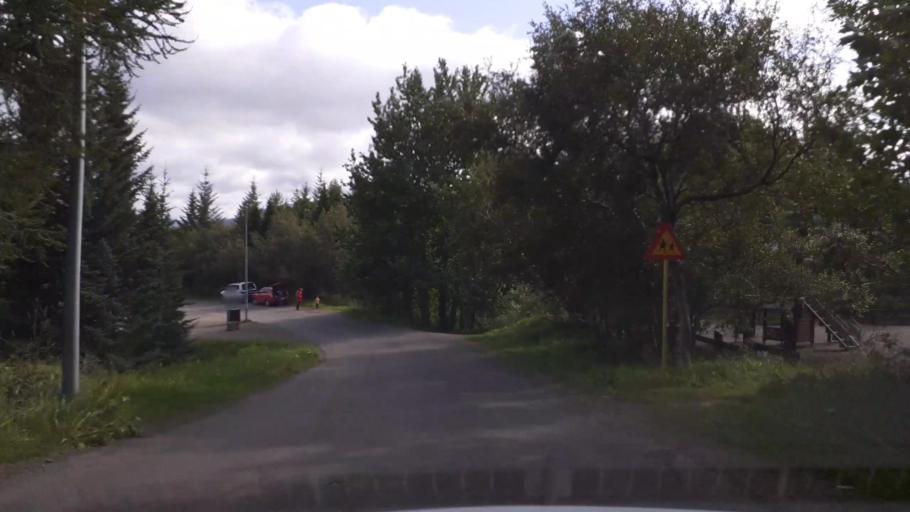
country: IS
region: Northeast
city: Akureyri
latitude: 65.6471
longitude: -18.0870
